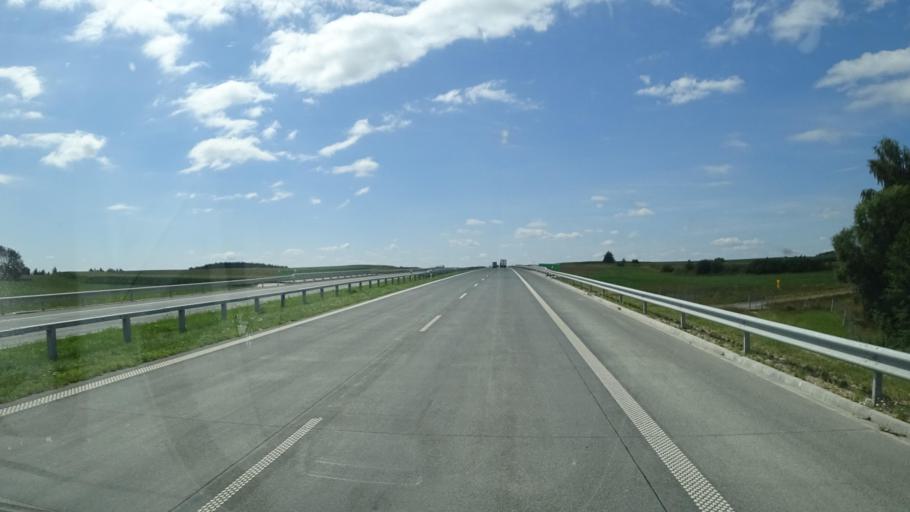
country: PL
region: Podlasie
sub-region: Powiat grajewski
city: Szczuczyn
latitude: 53.5116
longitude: 22.2458
